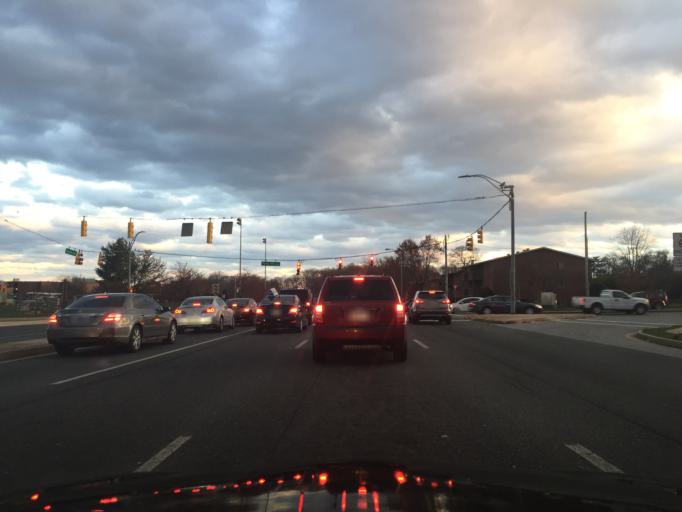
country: US
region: Maryland
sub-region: Baltimore County
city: Towson
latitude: 39.3935
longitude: -76.5840
